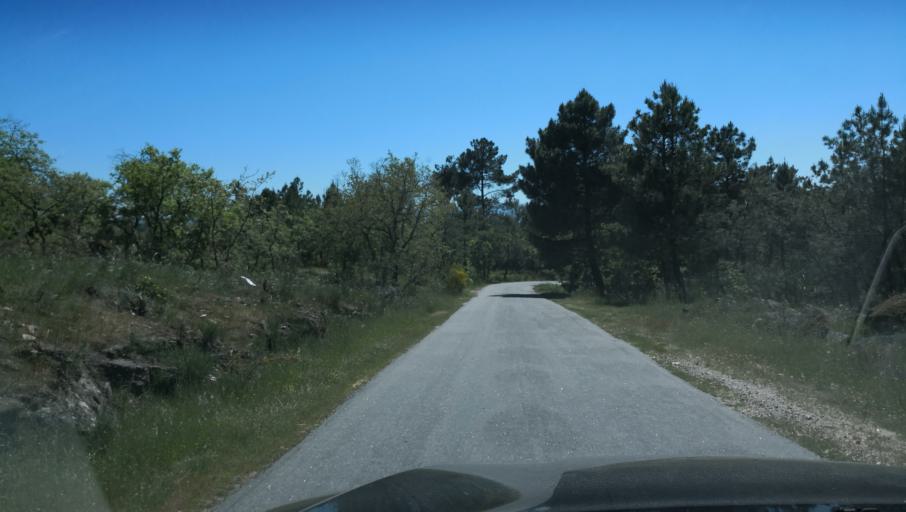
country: PT
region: Vila Real
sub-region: Vila Real
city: Vila Real
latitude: 41.2928
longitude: -7.6610
